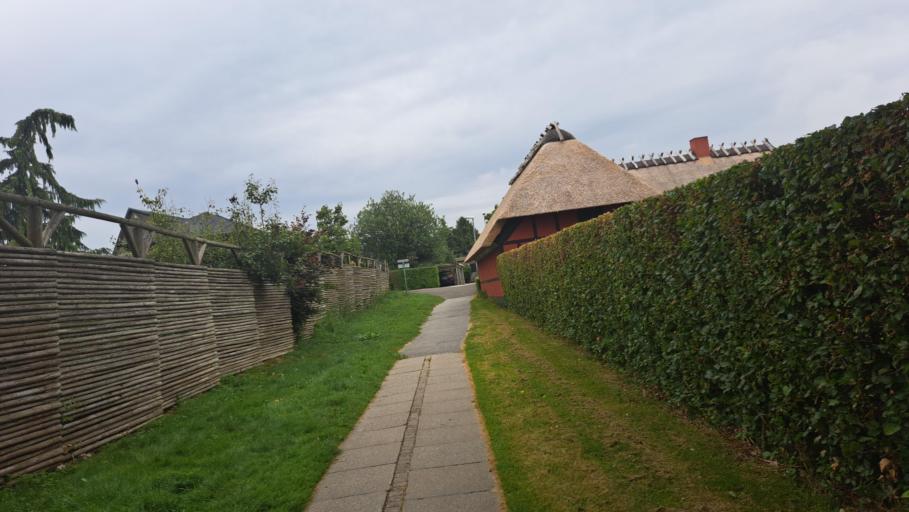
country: DK
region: Central Jutland
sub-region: Hedensted Kommune
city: Hedensted
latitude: 55.7714
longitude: 9.7068
